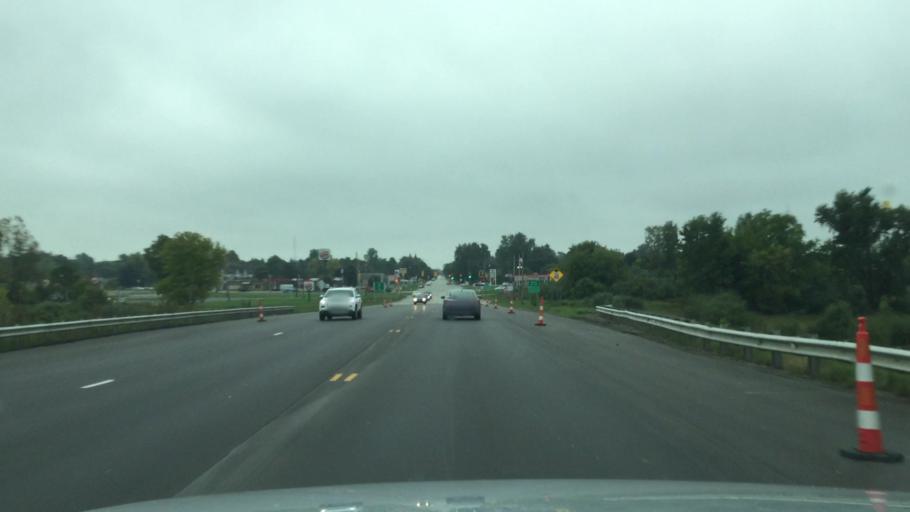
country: US
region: Michigan
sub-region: Shiawassee County
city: Perry
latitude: 42.8392
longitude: -84.2198
